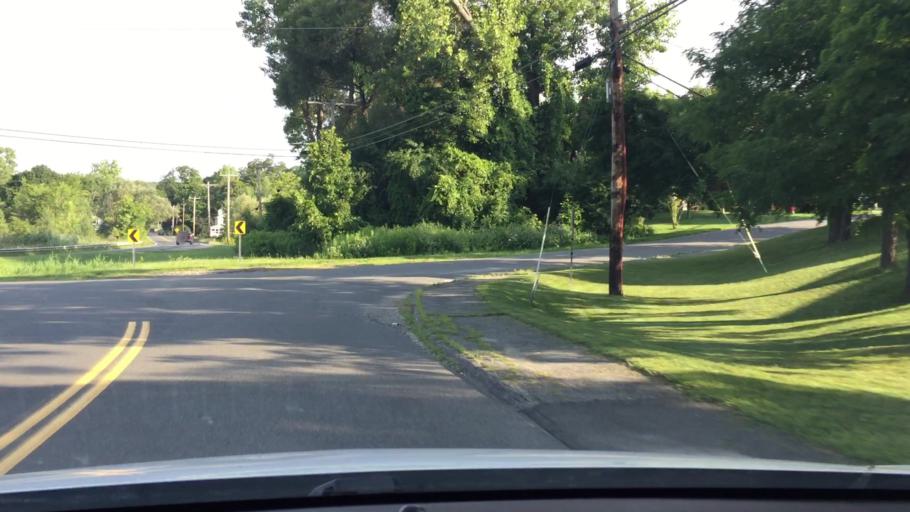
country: US
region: Massachusetts
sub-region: Berkshire County
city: Lee
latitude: 42.3255
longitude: -73.2394
